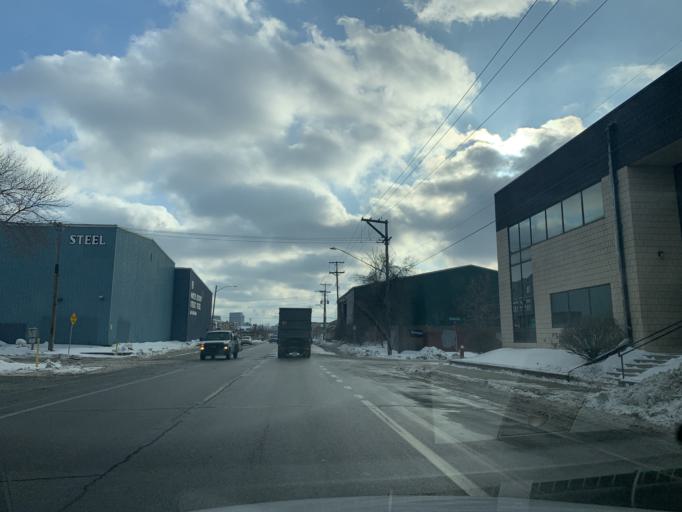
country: US
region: Minnesota
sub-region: Hennepin County
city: Minneapolis
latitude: 45.0029
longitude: -93.2802
